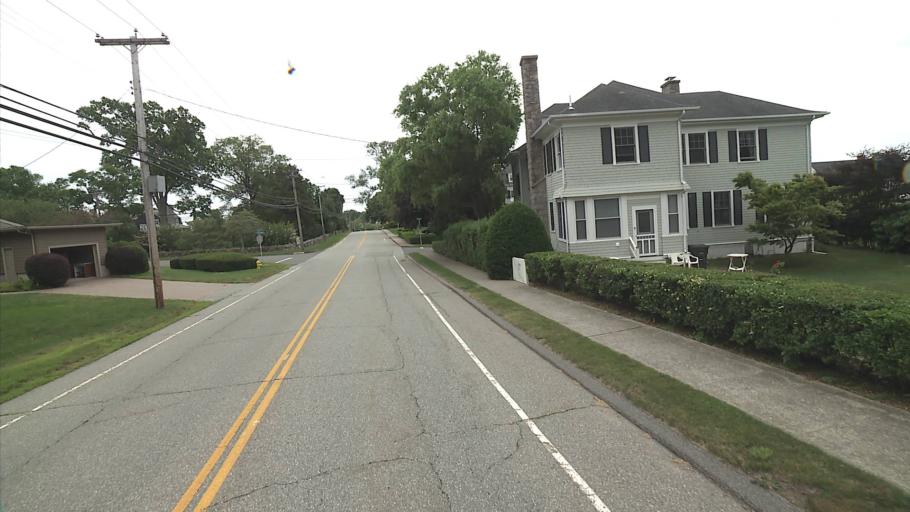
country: US
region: Connecticut
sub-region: New London County
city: Groton
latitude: 41.3225
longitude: -72.0698
